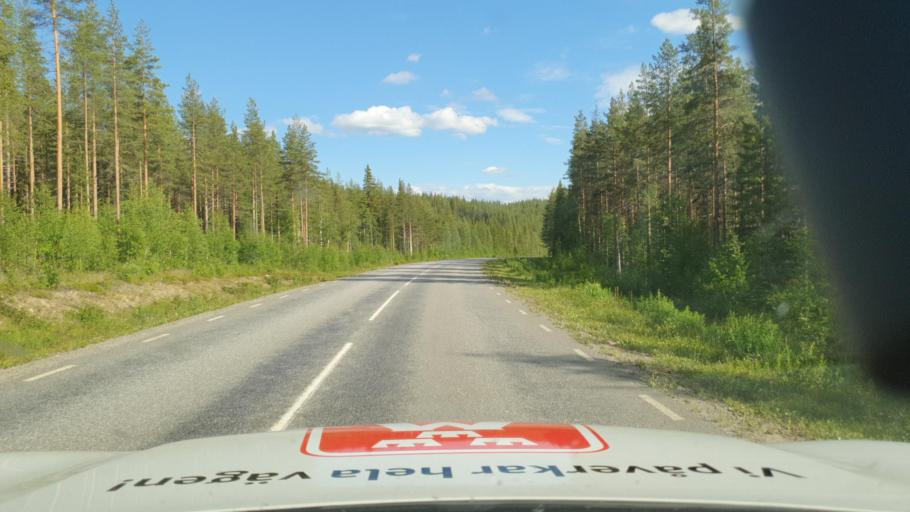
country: SE
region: Vaesterbotten
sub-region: Norsjo Kommun
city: Norsjoe
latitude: 64.8699
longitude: 19.7212
